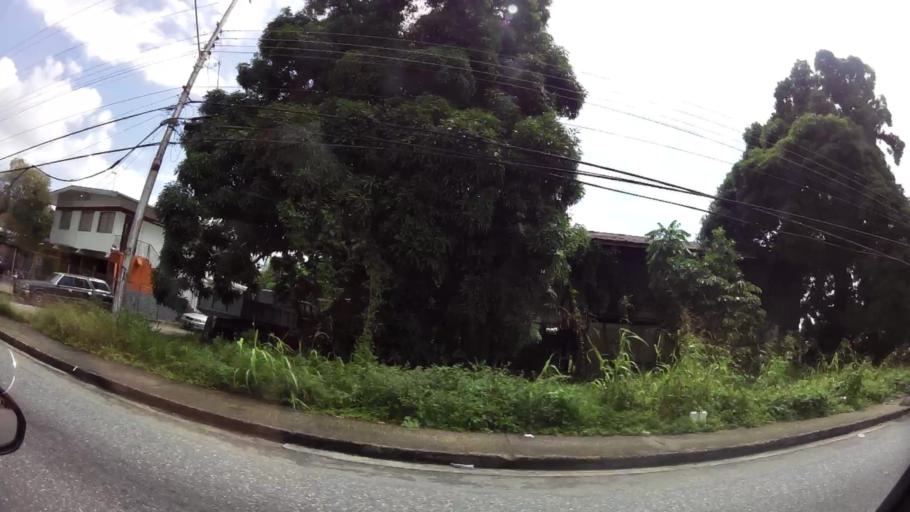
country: TT
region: Borough of Arima
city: Arima
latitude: 10.6343
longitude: -61.2924
